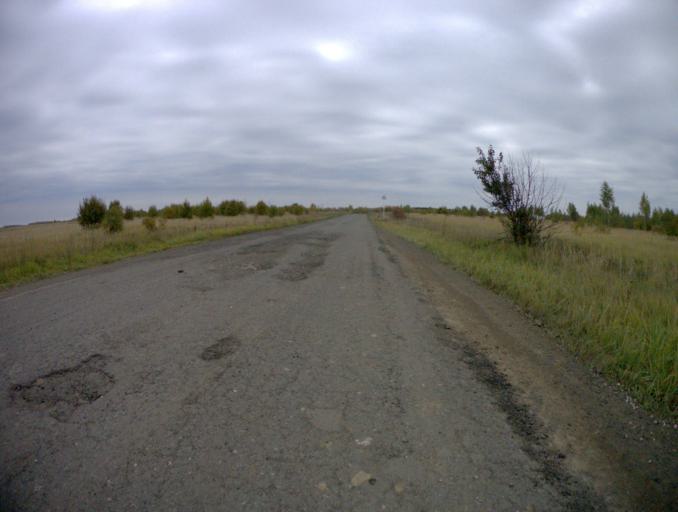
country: RU
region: Vladimir
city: Mstera
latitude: 56.3801
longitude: 41.8937
